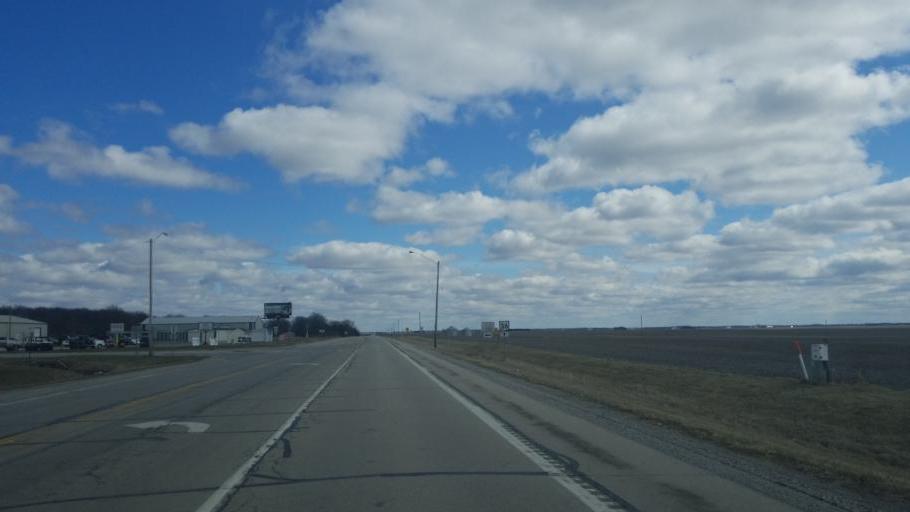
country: US
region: Illinois
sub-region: Douglas County
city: Villa Grove
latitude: 39.7917
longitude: -88.1610
